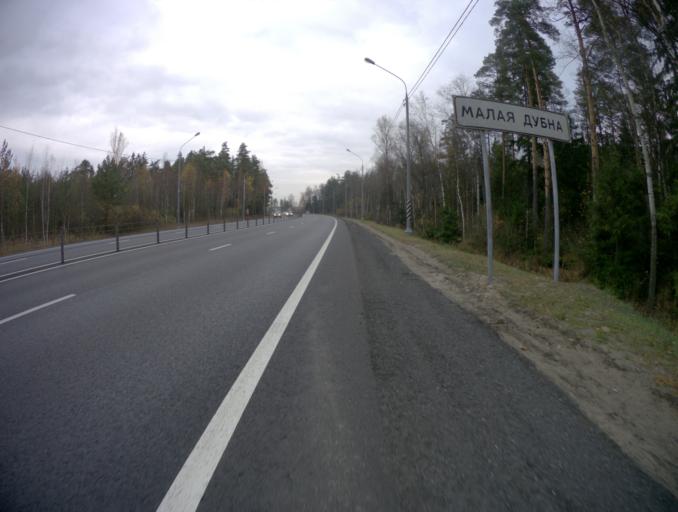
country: RU
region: Moskovskaya
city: Malaya Dubna
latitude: 55.8672
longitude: 38.9640
